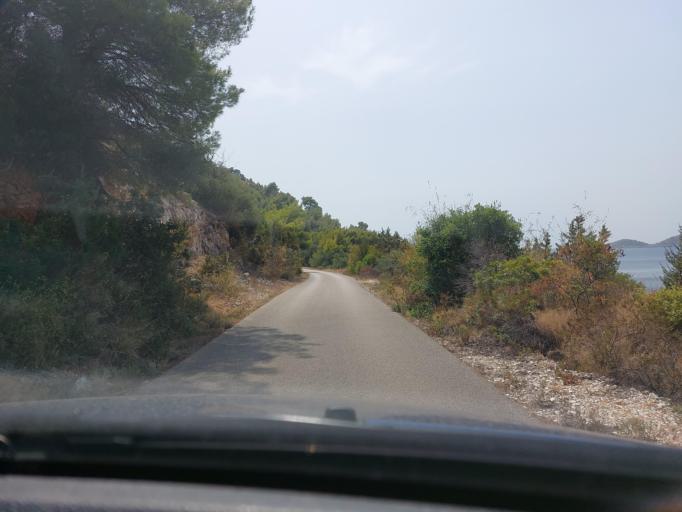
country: HR
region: Dubrovacko-Neretvanska
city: Smokvica
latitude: 42.7304
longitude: 16.8912
